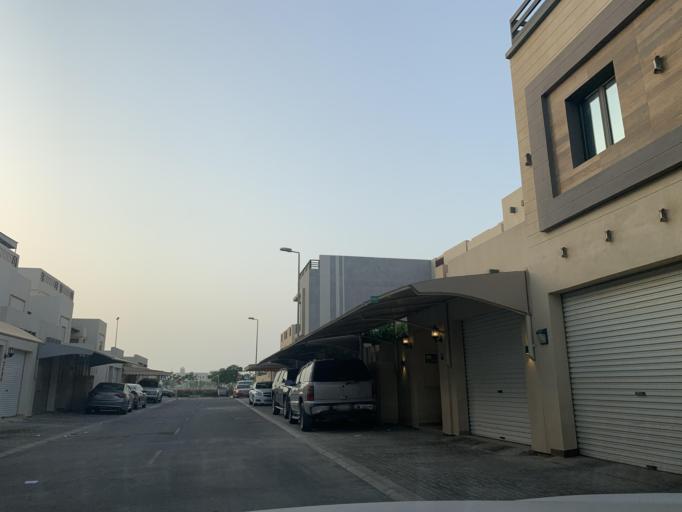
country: BH
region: Manama
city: Jidd Hafs
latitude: 26.2227
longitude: 50.4451
